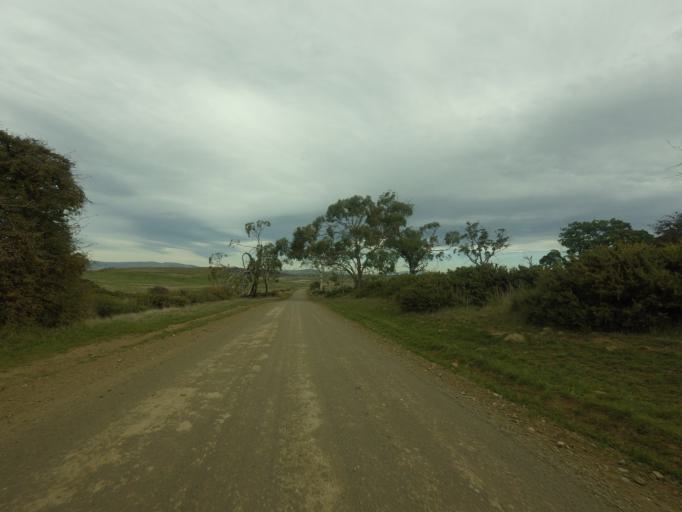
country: AU
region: Tasmania
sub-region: Derwent Valley
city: New Norfolk
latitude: -42.3895
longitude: 146.9775
